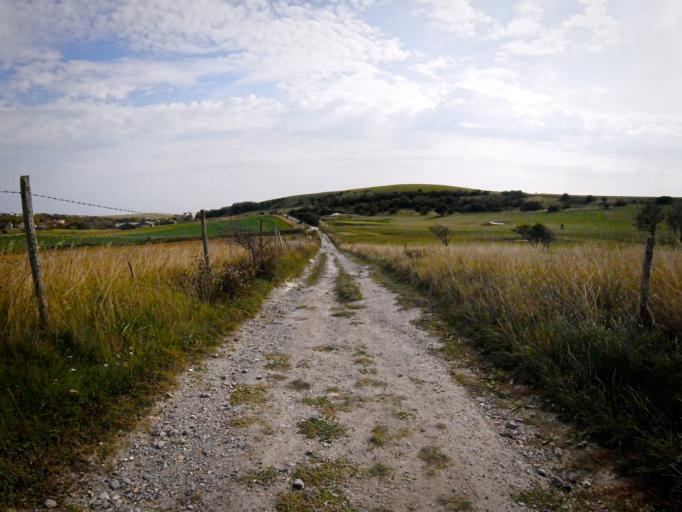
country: GB
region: England
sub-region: Brighton and Hove
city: Rottingdean
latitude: 50.8216
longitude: -0.0843
